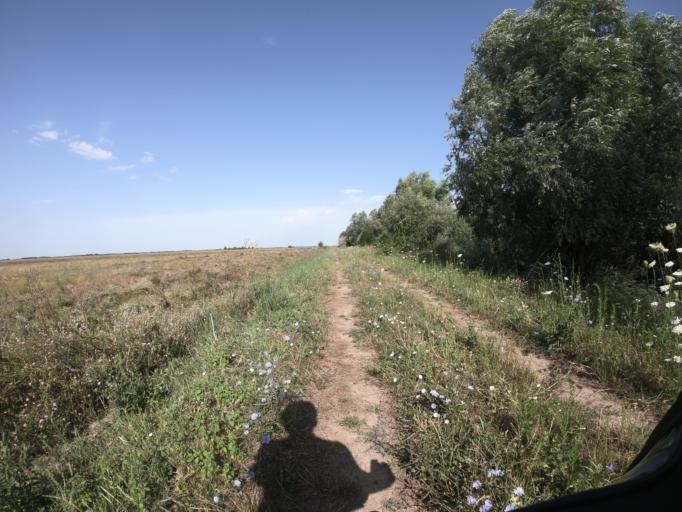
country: HU
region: Hajdu-Bihar
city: Egyek
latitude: 47.5779
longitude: 20.9259
